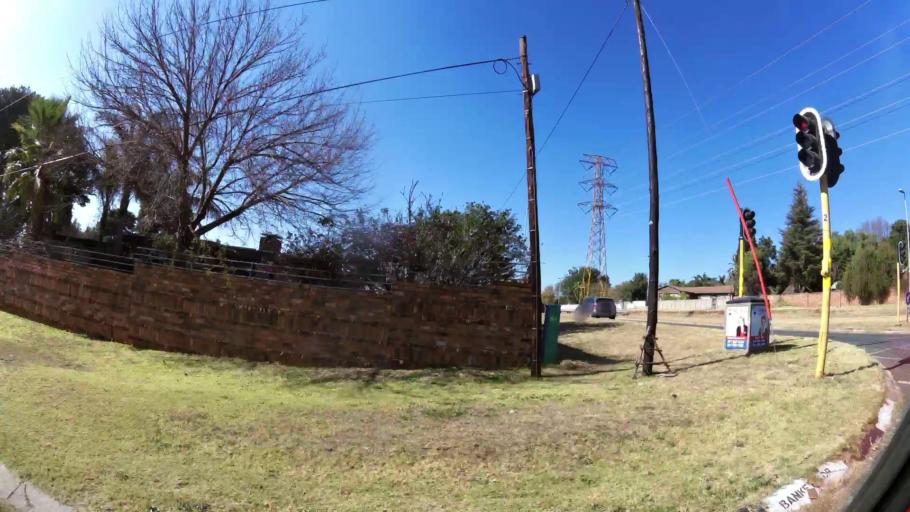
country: ZA
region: Gauteng
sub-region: City of Johannesburg Metropolitan Municipality
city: Roodepoort
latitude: -26.1195
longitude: 27.8582
